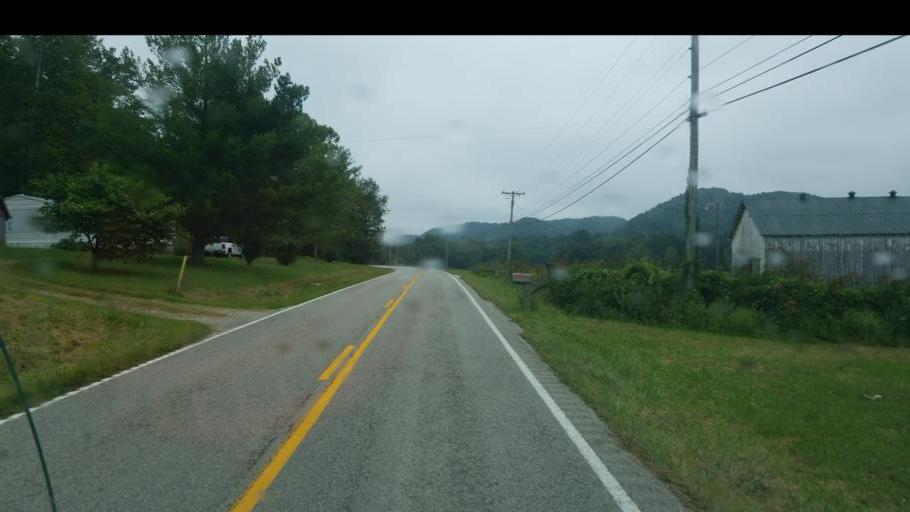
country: US
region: Kentucky
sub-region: Rowan County
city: Morehead
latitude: 38.2647
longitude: -83.4326
